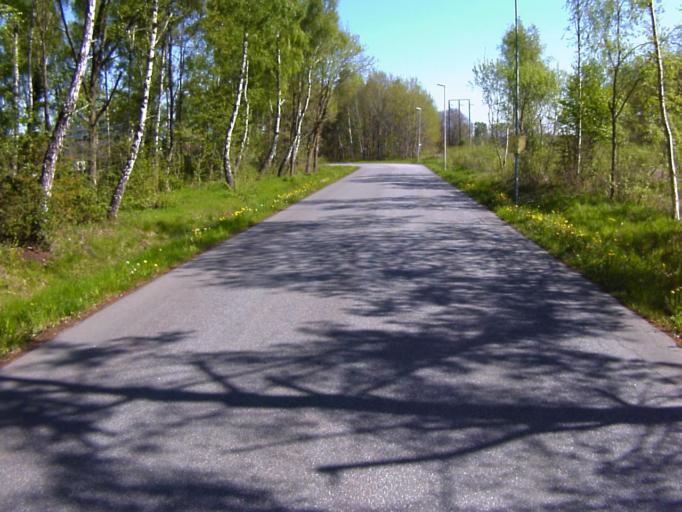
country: SE
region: Skane
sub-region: Kristianstads Kommun
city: Onnestad
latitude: 55.9407
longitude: 13.9862
